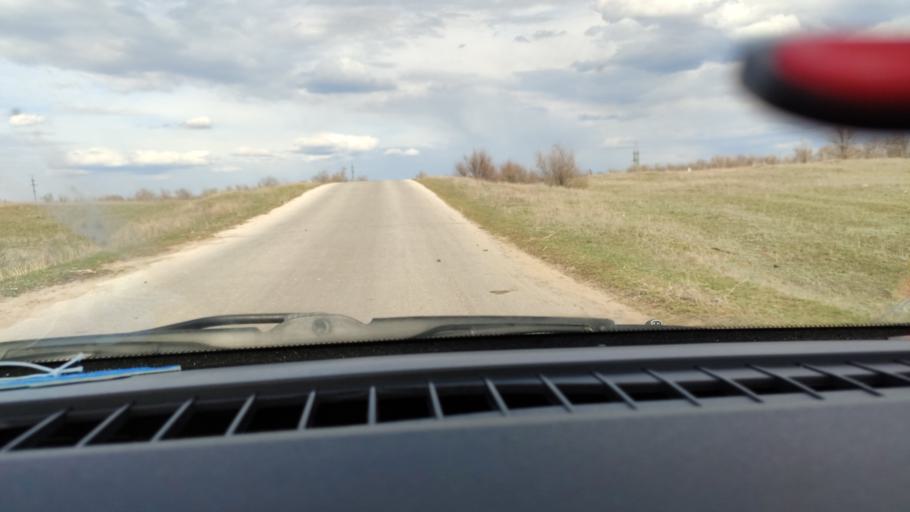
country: RU
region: Saratov
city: Rovnoye
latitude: 50.9412
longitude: 46.1279
